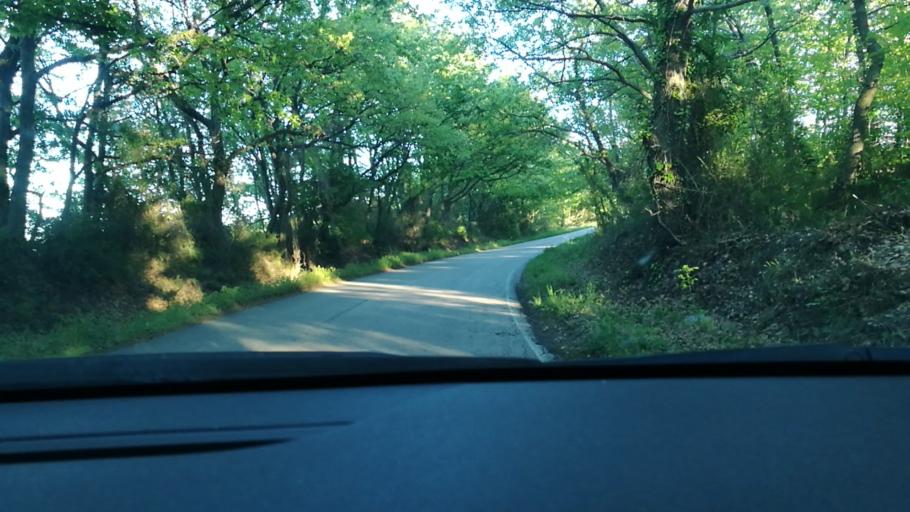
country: IT
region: Molise
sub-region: Provincia di Campobasso
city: Petacciato
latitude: 42.0033
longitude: 14.8823
